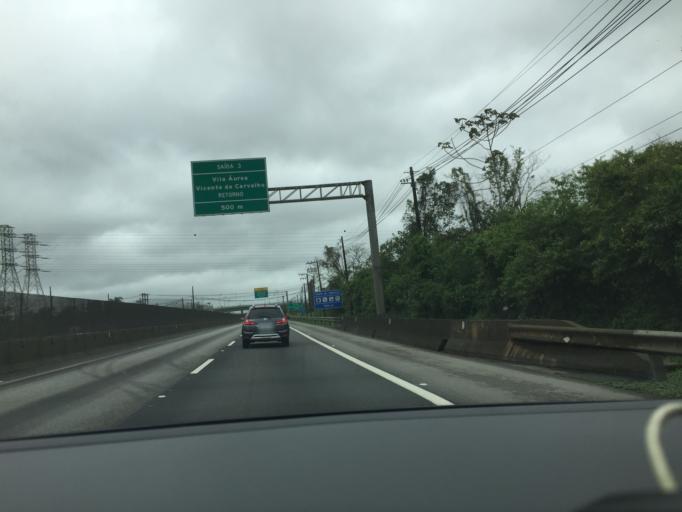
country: BR
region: Sao Paulo
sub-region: Santos
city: Santos
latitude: -23.9326
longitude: -46.2835
